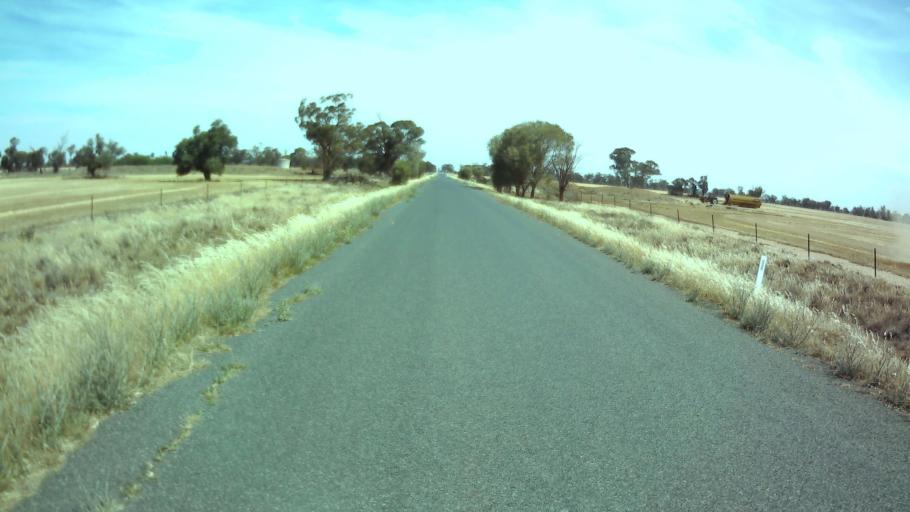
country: AU
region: New South Wales
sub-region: Weddin
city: Grenfell
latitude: -33.9923
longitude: 147.7758
